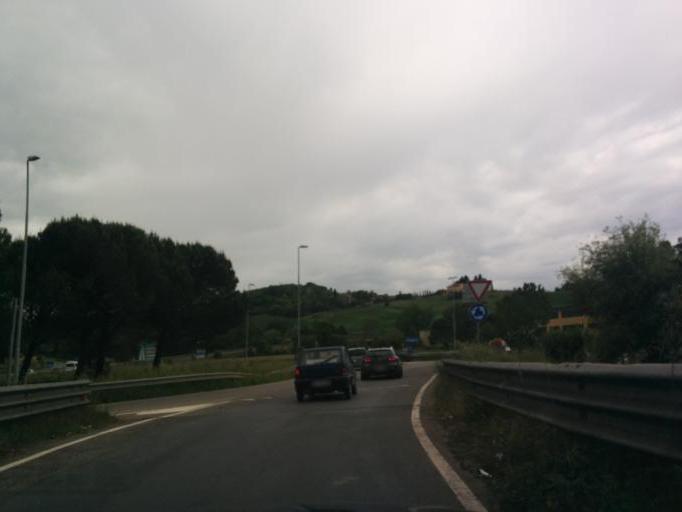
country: IT
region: Tuscany
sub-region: Provincia di Siena
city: Poggibonsi
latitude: 43.4864
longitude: 11.1498
